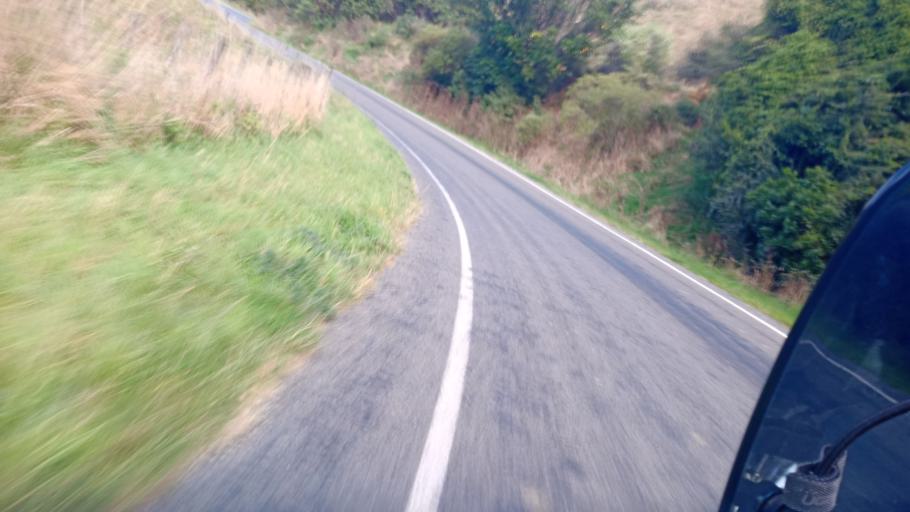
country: NZ
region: Gisborne
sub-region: Gisborne District
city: Gisborne
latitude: -38.5318
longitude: 177.5520
